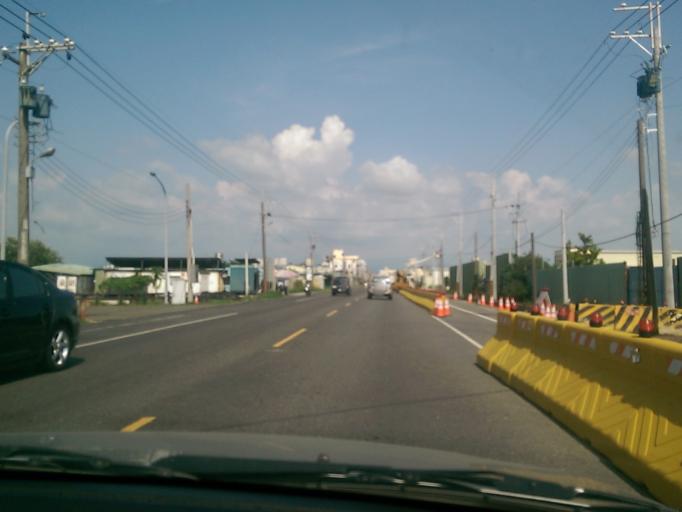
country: TW
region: Taiwan
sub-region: Chiayi
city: Taibao
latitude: 23.5583
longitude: 120.3378
